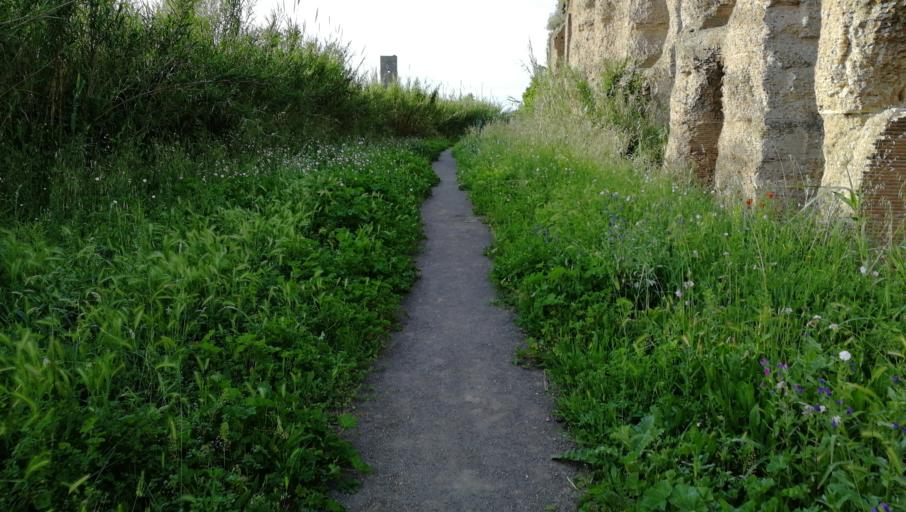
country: IT
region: Latium
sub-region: Citta metropolitana di Roma Capitale
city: Rome
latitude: 41.8581
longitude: 12.5440
